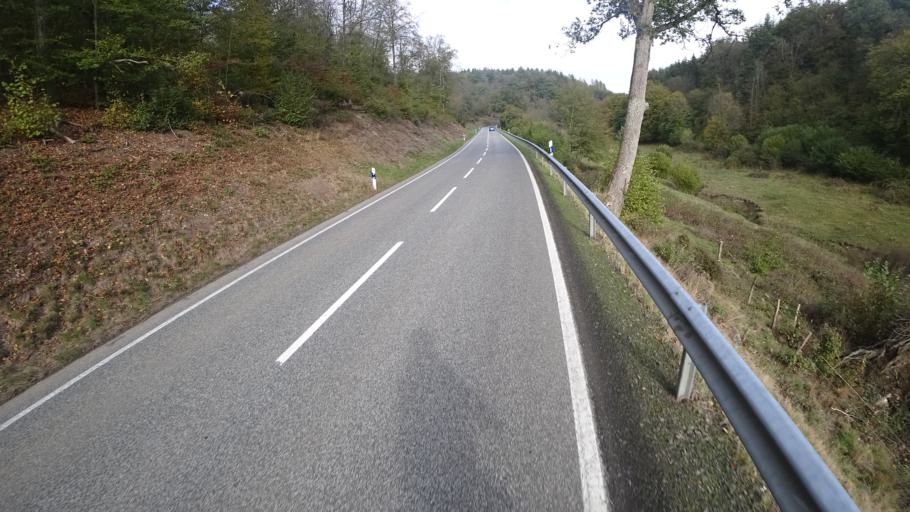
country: DE
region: Rheinland-Pfalz
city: Isselbach
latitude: 50.3988
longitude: 7.9123
